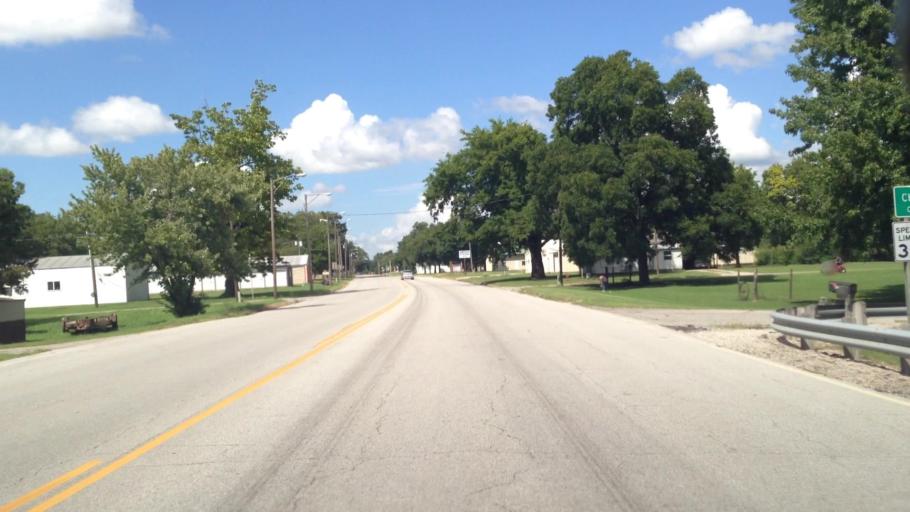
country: US
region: Kansas
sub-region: Labette County
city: Chetopa
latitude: 37.0310
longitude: -95.0861
